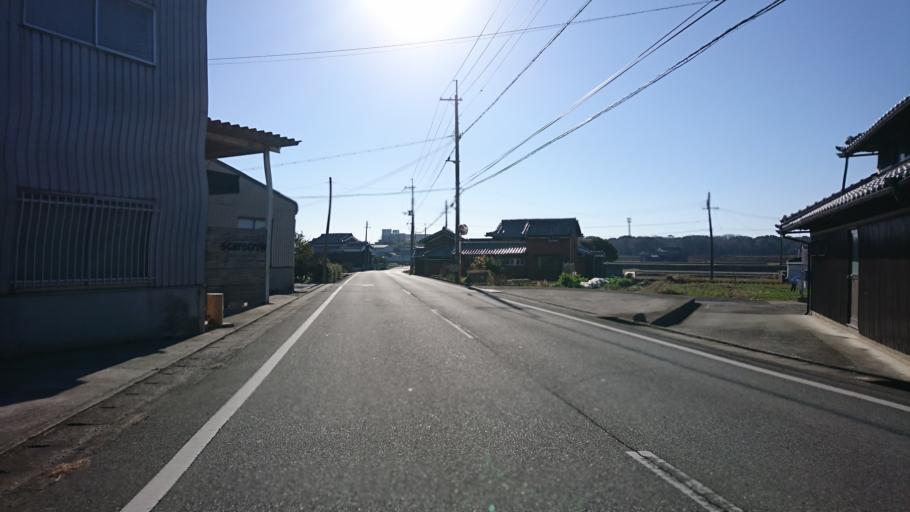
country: JP
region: Hyogo
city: Miki
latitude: 34.7594
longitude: 134.9240
